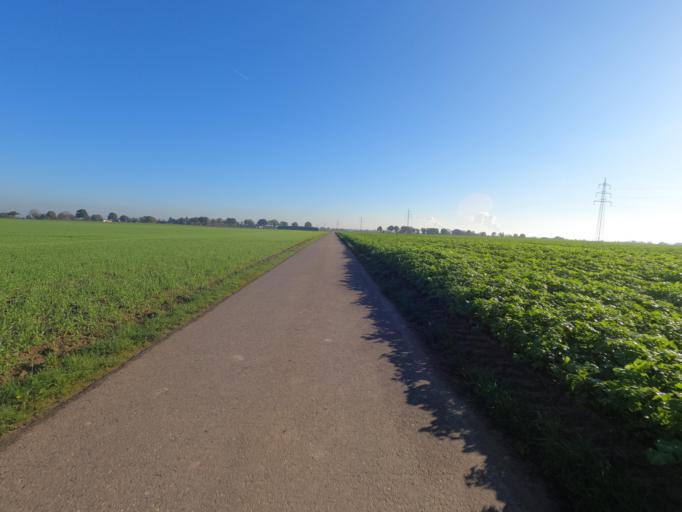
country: DE
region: North Rhine-Westphalia
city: Erkelenz
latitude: 51.0857
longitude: 6.3553
